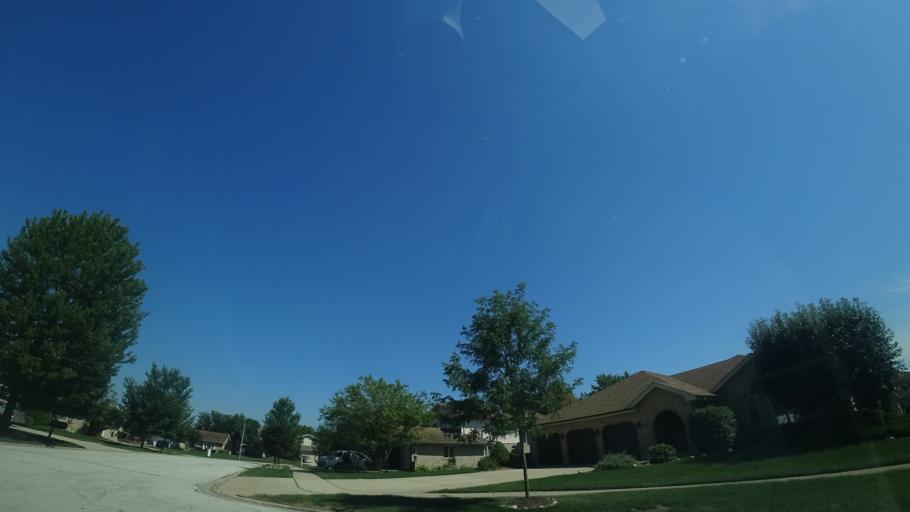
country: US
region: Illinois
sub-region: Will County
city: Homer Glen
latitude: 41.5704
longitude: -87.9058
